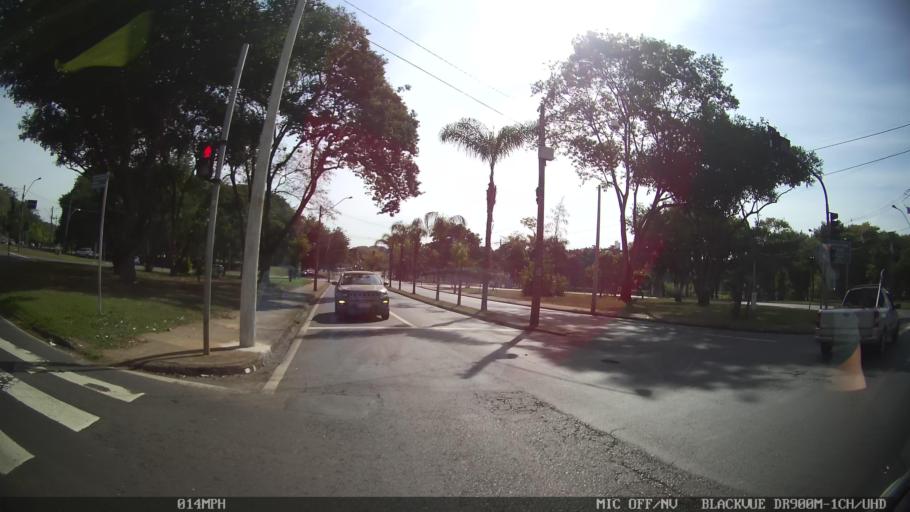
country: BR
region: Sao Paulo
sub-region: Piracicaba
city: Piracicaba
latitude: -22.7284
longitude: -47.6659
